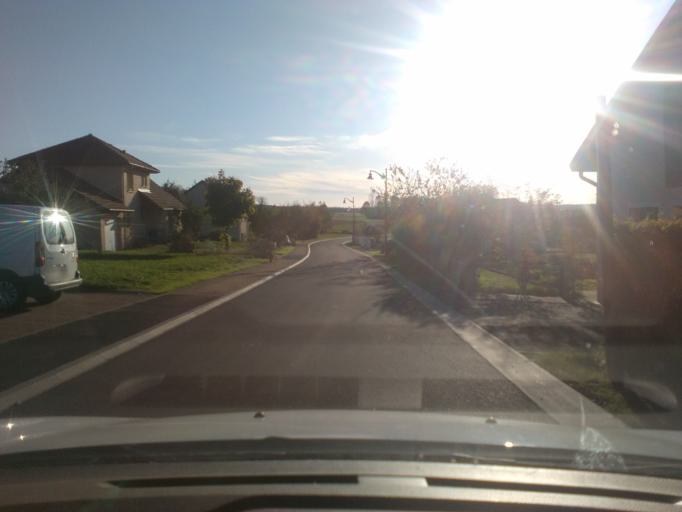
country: FR
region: Lorraine
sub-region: Departement des Vosges
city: Rambervillers
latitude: 48.2936
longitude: 6.6008
